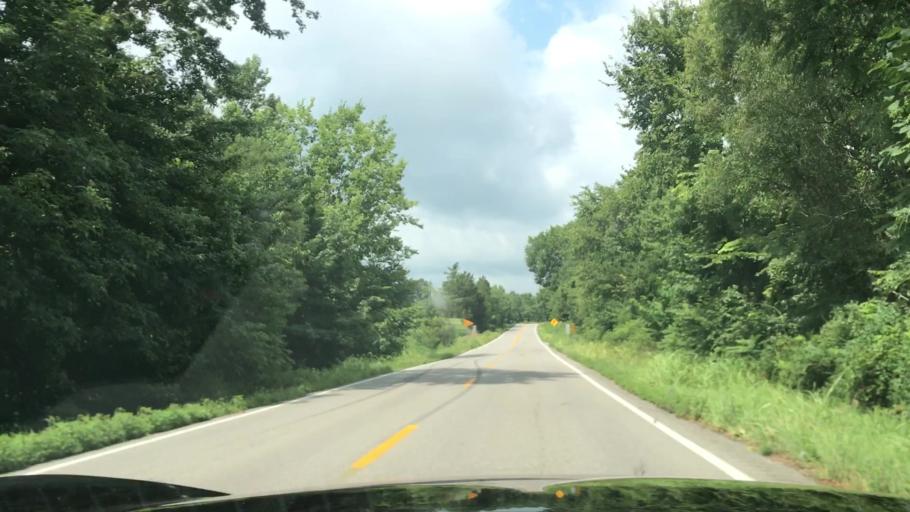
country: US
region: Kentucky
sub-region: Muhlenberg County
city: Central City
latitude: 37.1963
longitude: -86.9845
